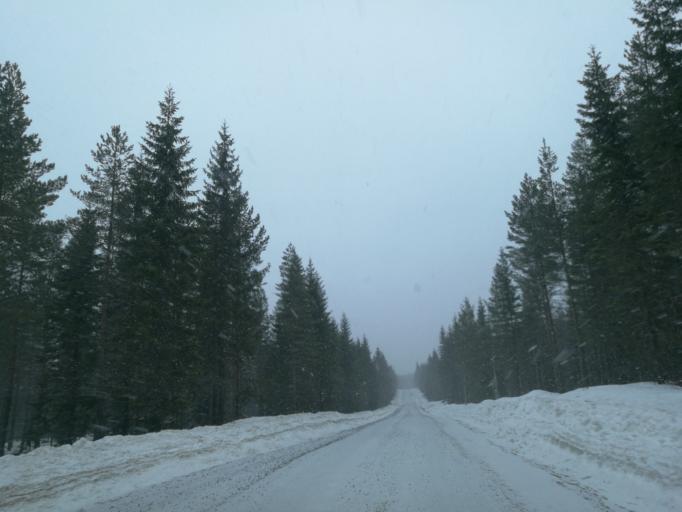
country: SE
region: Vaermland
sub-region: Torsby Kommun
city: Torsby
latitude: 60.6581
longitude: 12.8080
